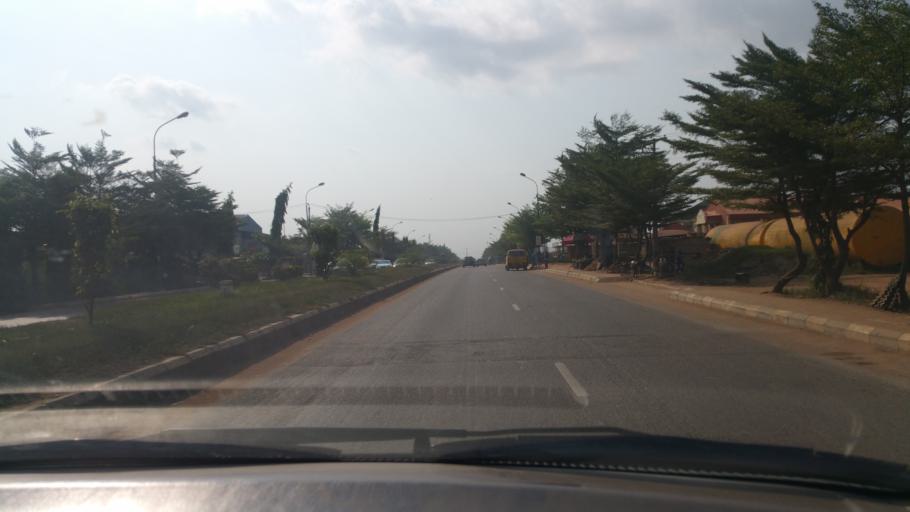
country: NG
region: Lagos
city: Ikotun
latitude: 6.5771
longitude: 3.2707
